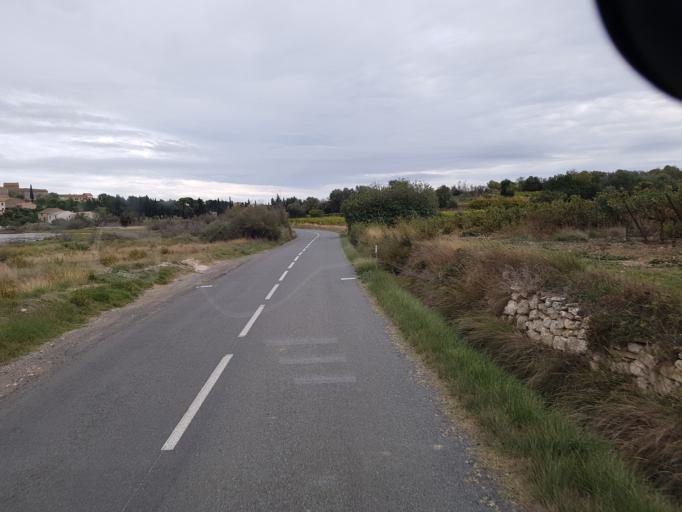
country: FR
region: Languedoc-Roussillon
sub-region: Departement de l'Aude
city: Peyriac-de-Mer
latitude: 43.1263
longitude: 2.9870
